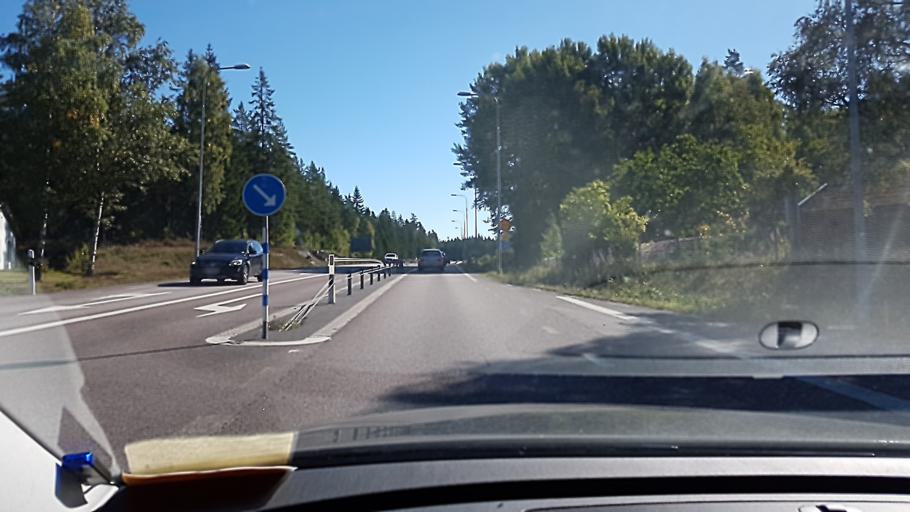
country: SE
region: Kalmar
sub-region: Emmaboda Kommun
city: Emmaboda
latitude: 56.7194
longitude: 15.6867
